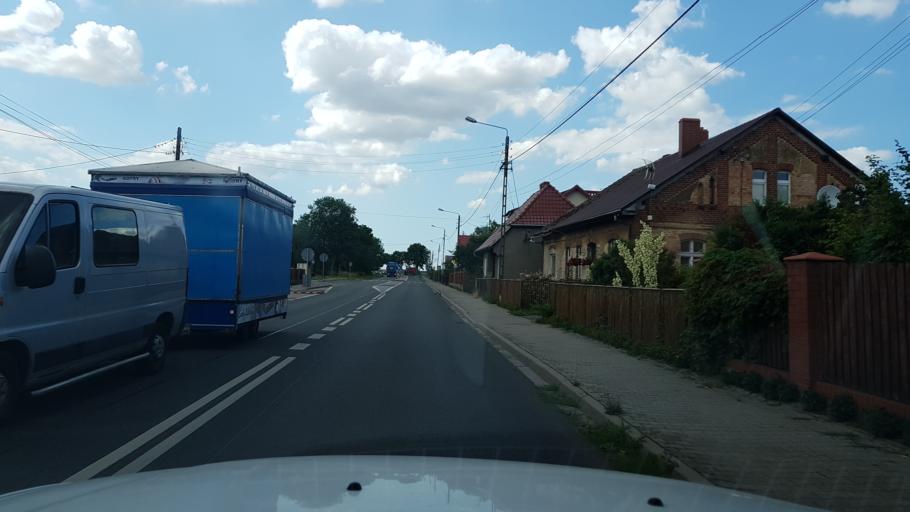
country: PL
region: West Pomeranian Voivodeship
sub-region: Powiat pyrzycki
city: Pyrzyce
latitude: 53.1871
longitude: 14.8393
